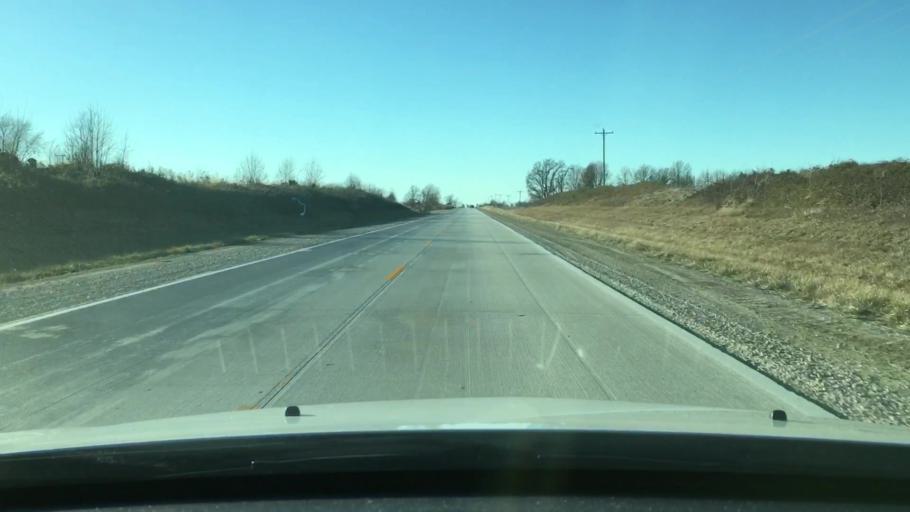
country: US
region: Missouri
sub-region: Boone County
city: Centralia
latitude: 39.2020
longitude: -92.0692
